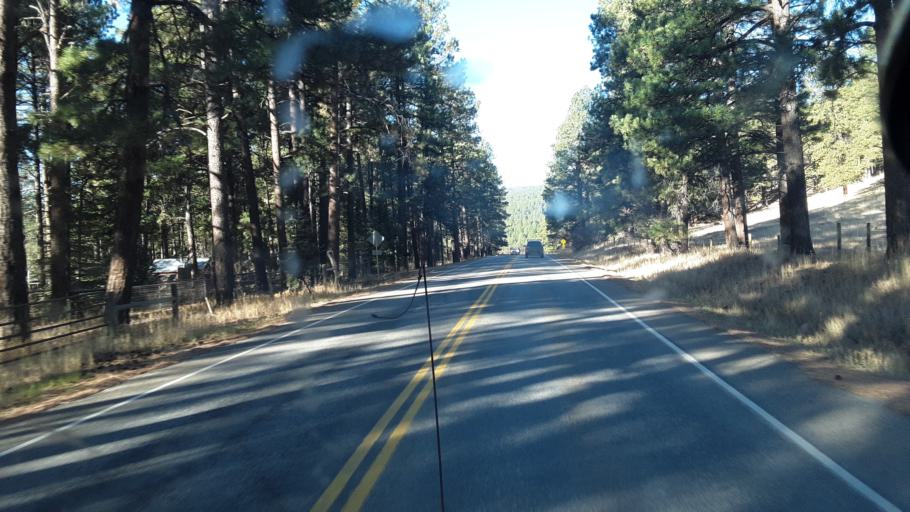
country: US
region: Colorado
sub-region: La Plata County
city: Durango
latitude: 37.3310
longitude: -107.7335
